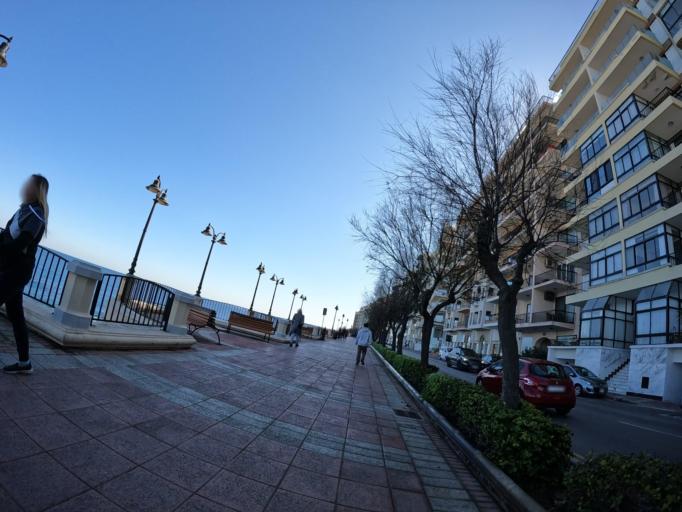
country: MT
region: Tas-Sliema
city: Sliema
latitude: 35.9175
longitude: 14.4998
